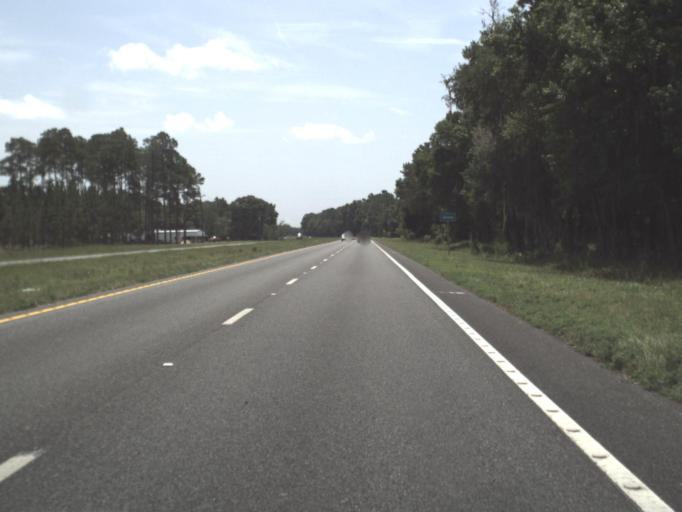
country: US
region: Florida
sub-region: Taylor County
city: Perry
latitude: 29.9873
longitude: -83.4960
